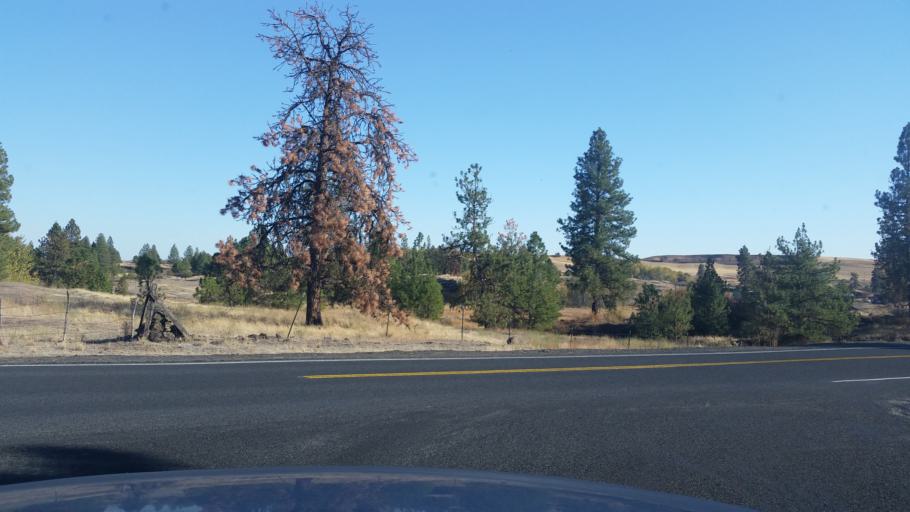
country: US
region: Washington
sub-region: Spokane County
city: Cheney
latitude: 47.3575
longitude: -117.6867
